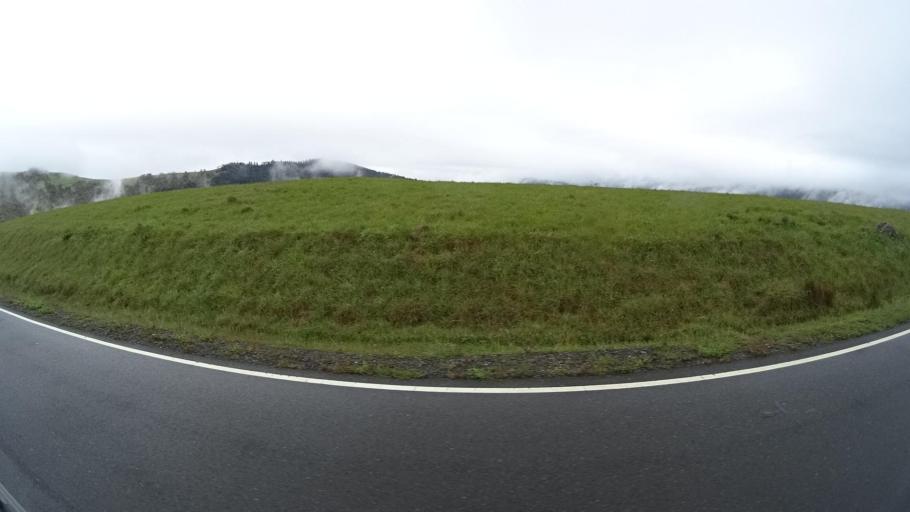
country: US
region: California
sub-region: Humboldt County
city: Westhaven-Moonstone
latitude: 41.1649
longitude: -123.9088
